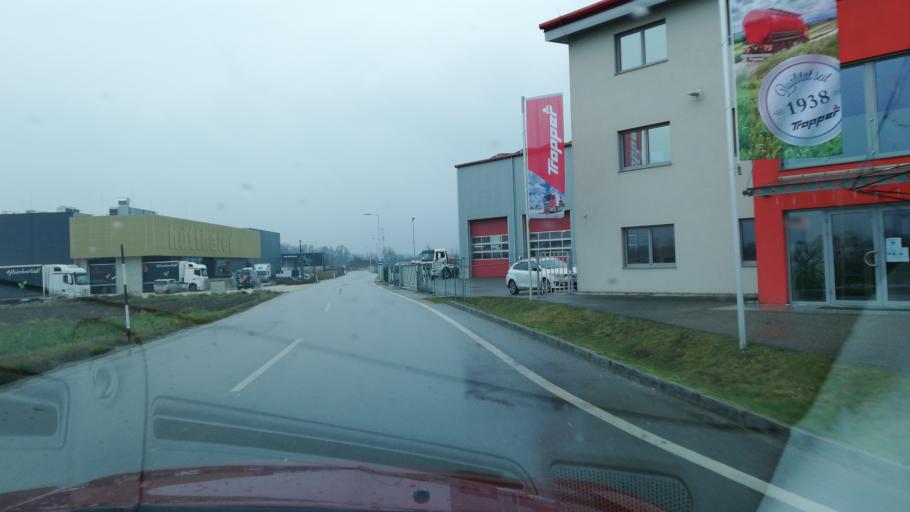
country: AT
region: Upper Austria
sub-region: Politischer Bezirk Vocklabruck
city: Oberndorf bei Schwanenstadt
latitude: 48.0452
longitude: 13.7600
